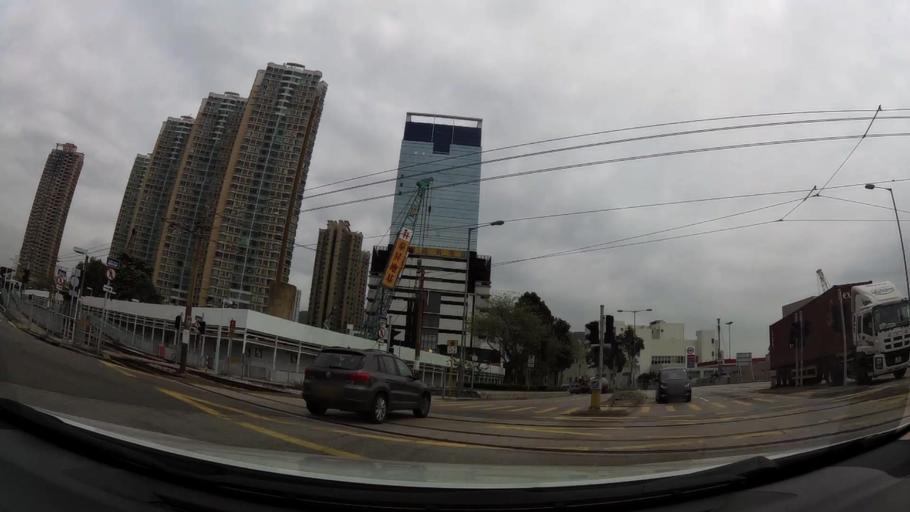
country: HK
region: Tuen Mun
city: Tuen Mun
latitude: 22.3807
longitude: 113.9702
